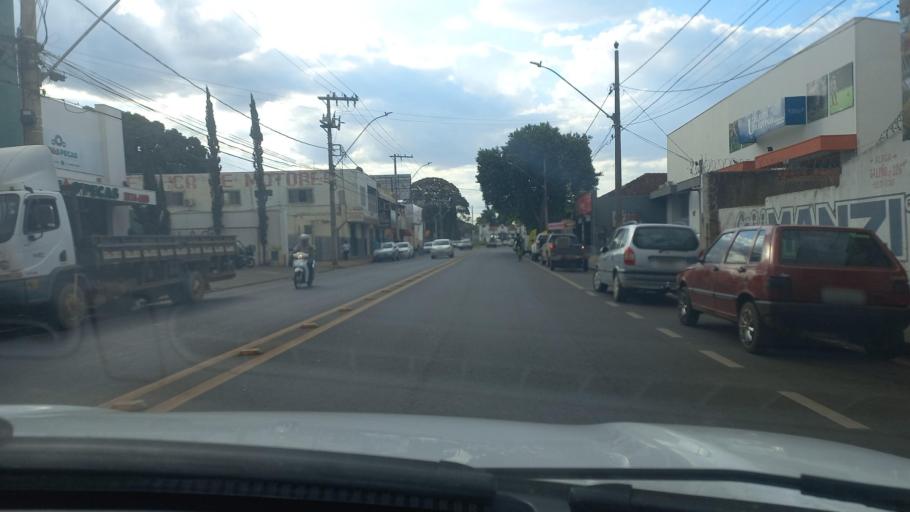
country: BR
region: Minas Gerais
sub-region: Uberaba
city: Uberaba
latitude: -19.7709
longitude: -47.9435
